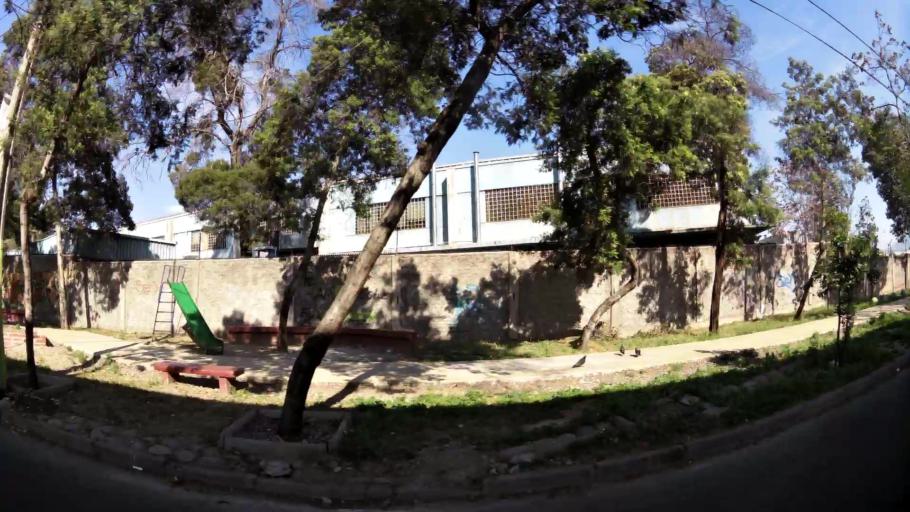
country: CL
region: Santiago Metropolitan
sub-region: Provincia de Santiago
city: Santiago
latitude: -33.4142
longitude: -70.6732
